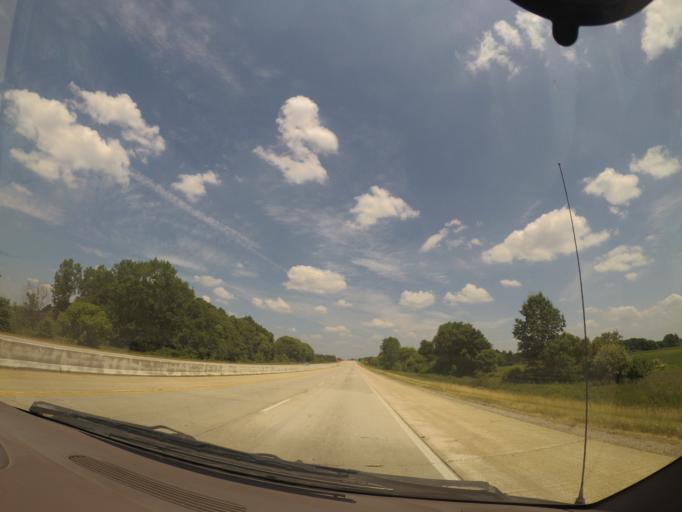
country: US
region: Indiana
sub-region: Elkhart County
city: Dunlap
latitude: 41.6428
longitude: -85.9610
